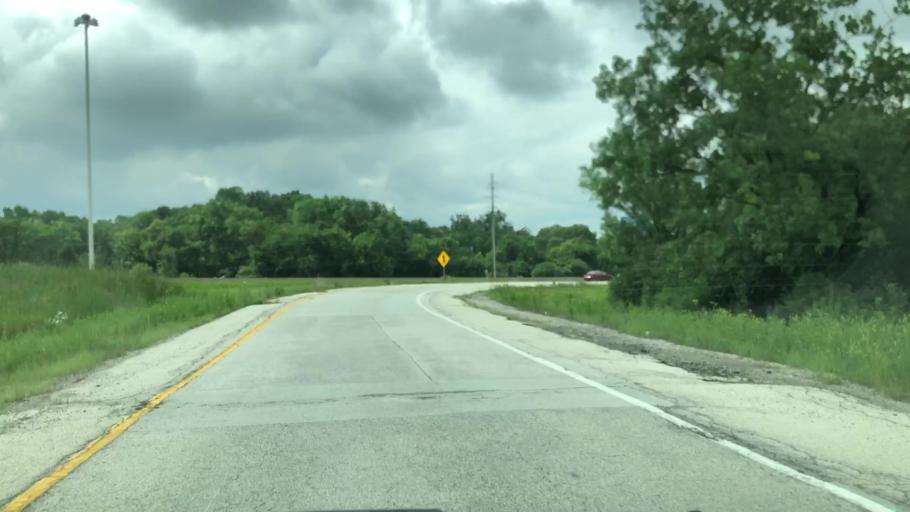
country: US
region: Illinois
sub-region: DuPage County
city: Oakbrook Terrace
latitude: 41.8628
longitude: -87.9583
